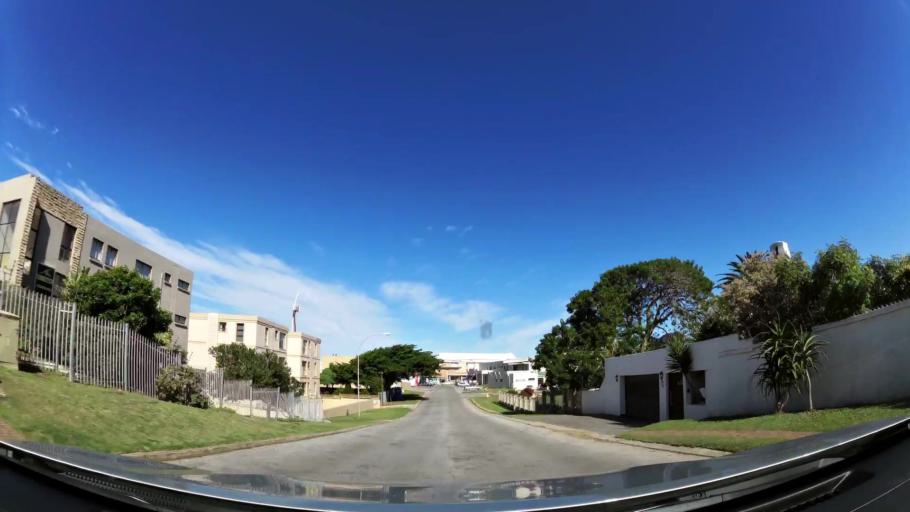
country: ZA
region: Eastern Cape
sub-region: Cacadu District Municipality
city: Jeffrey's Bay
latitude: -34.0507
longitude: 24.9243
